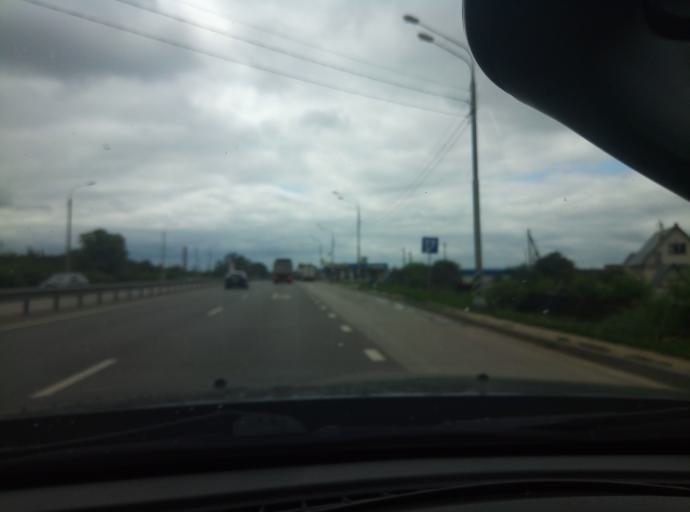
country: RU
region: Kaluga
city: Obninsk
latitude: 55.0763
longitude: 36.6279
